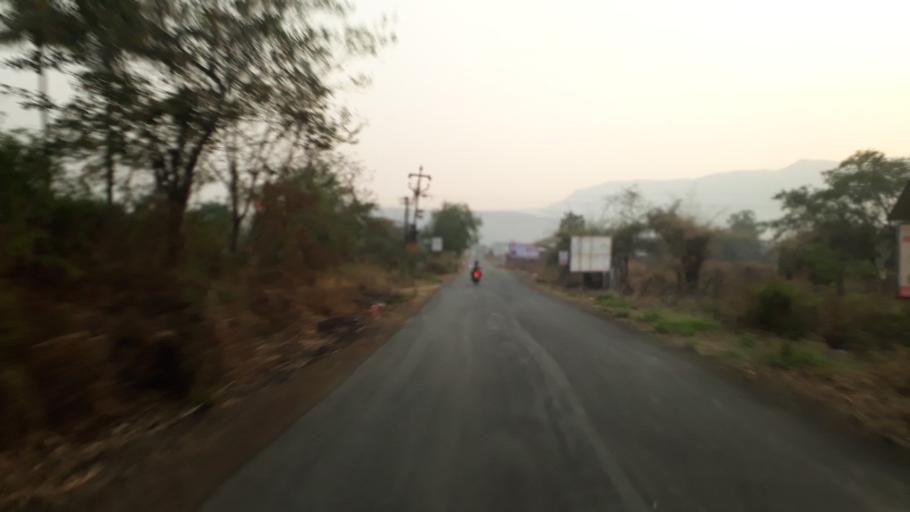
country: IN
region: Maharashtra
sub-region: Raigarh
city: Neral
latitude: 19.0379
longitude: 73.3286
